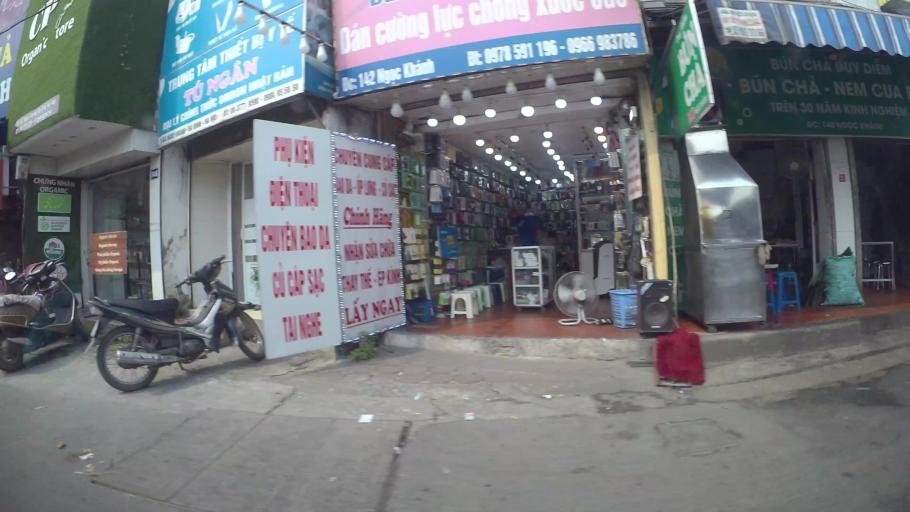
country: VN
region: Ha Noi
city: Dong Da
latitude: 21.0259
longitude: 105.8182
